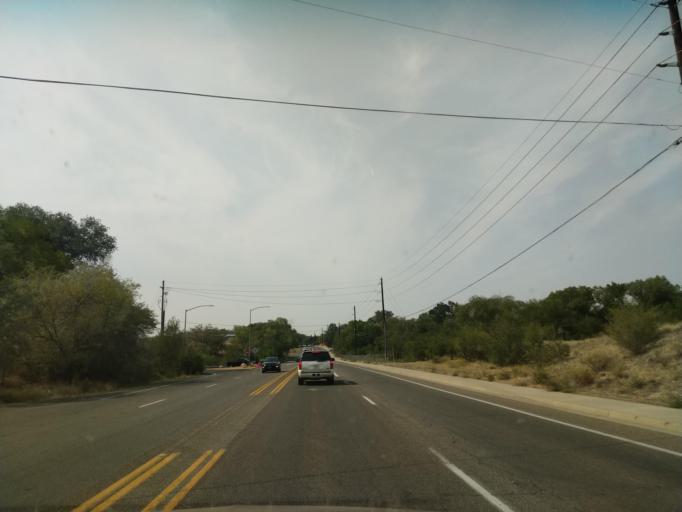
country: US
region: Colorado
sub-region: Mesa County
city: Redlands
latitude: 39.0663
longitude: -108.6008
